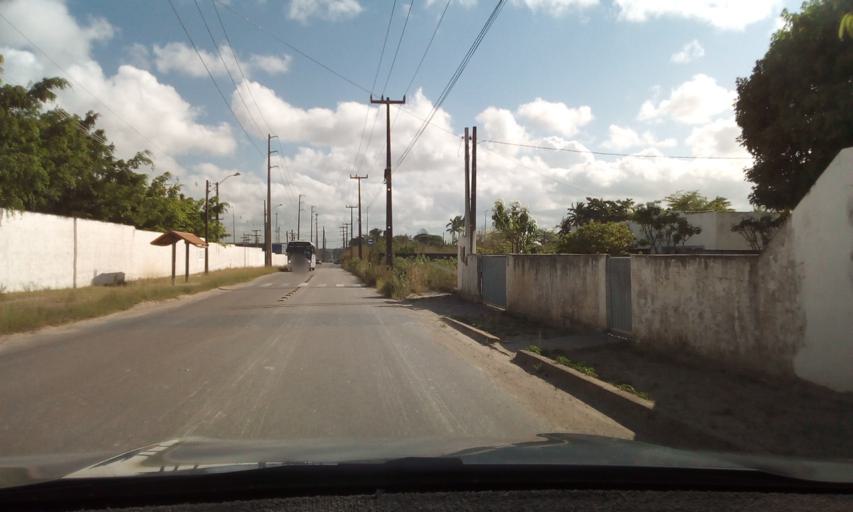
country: BR
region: Paraiba
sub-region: Bayeux
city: Bayeux
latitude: -7.1761
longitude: -34.9079
